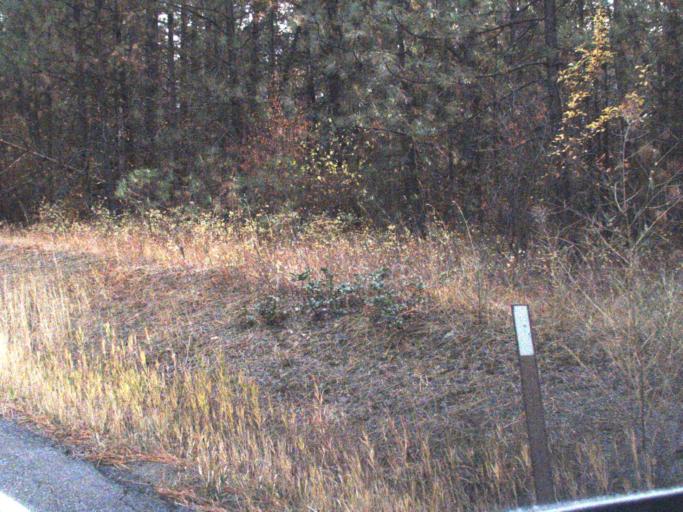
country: US
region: Washington
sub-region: Stevens County
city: Kettle Falls
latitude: 48.3009
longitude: -118.1479
